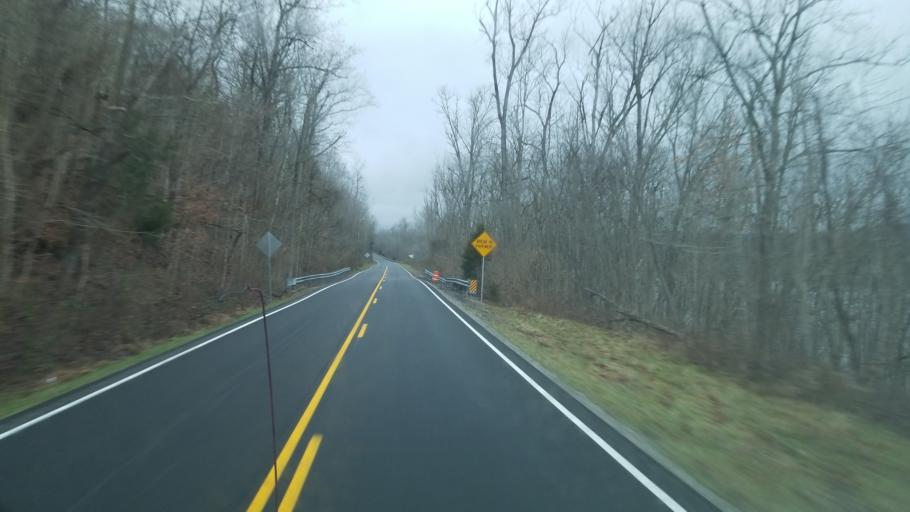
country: US
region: Kentucky
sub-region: Bracken County
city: Augusta
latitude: 38.7721
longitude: -83.9336
